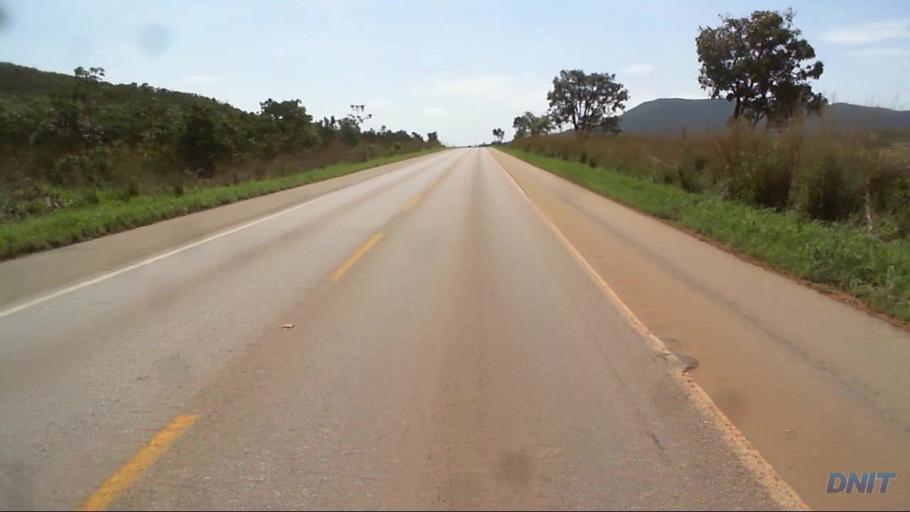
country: BR
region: Goias
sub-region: Barro Alto
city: Barro Alto
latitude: -15.1993
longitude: -48.7607
